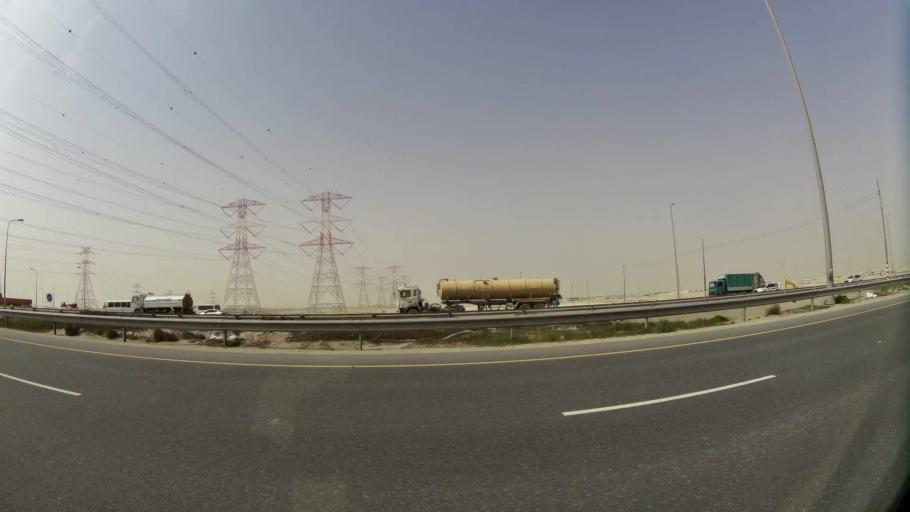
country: QA
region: Baladiyat ar Rayyan
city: Ar Rayyan
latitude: 25.1753
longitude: 51.3346
